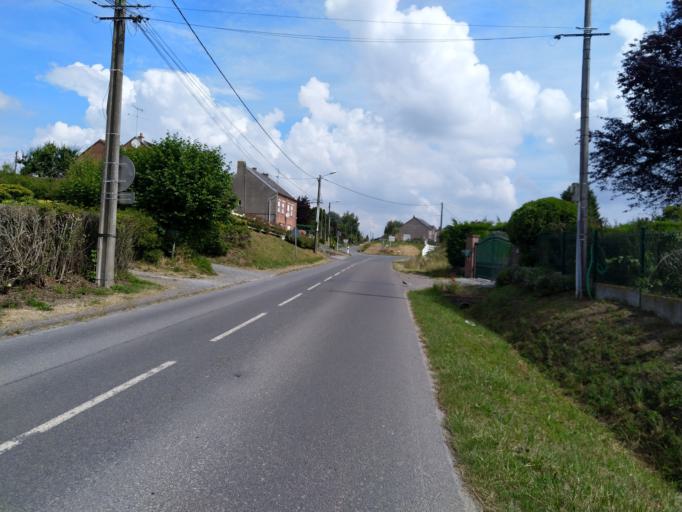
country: FR
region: Nord-Pas-de-Calais
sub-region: Departement du Nord
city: Rousies
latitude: 50.3019
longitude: 3.9959
